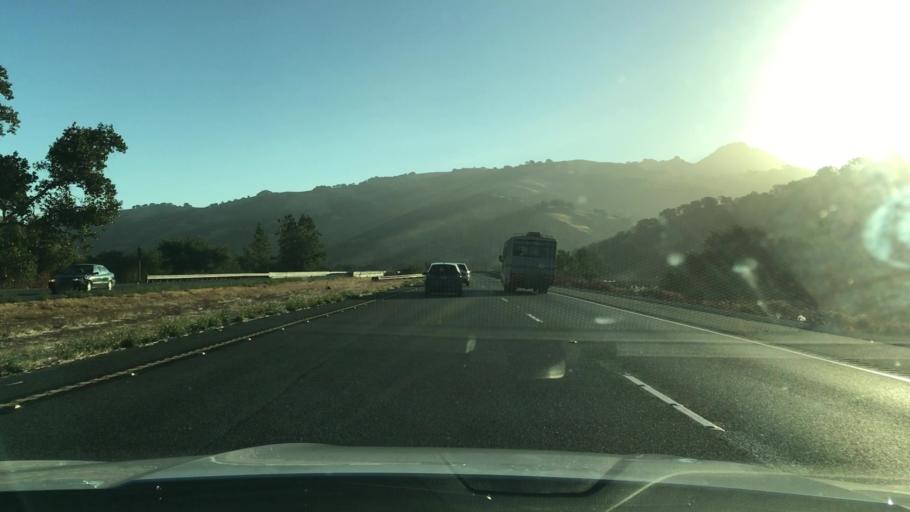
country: US
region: California
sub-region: San Benito County
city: Hollister
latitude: 37.0125
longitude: -121.3459
